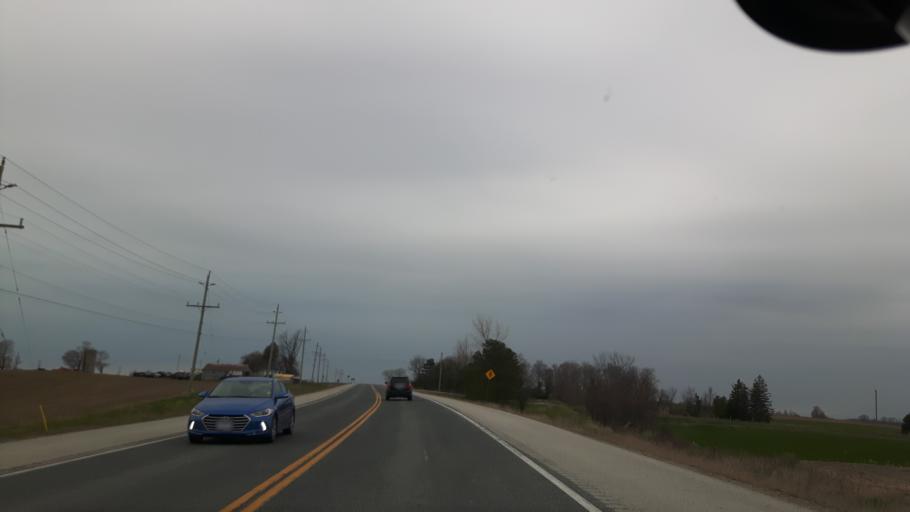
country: CA
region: Ontario
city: Goderich
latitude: 43.6902
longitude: -81.6333
